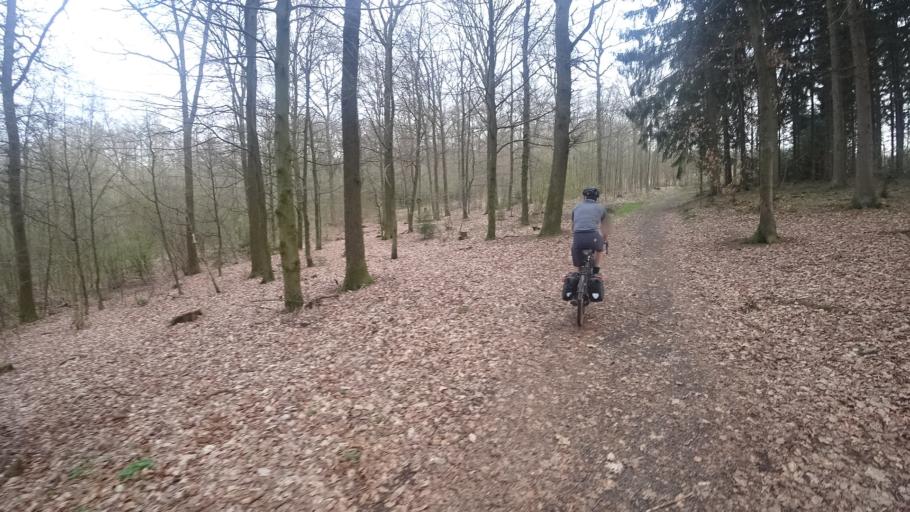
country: DE
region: Rheinland-Pfalz
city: Dickendorf
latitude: 50.7303
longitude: 7.8308
